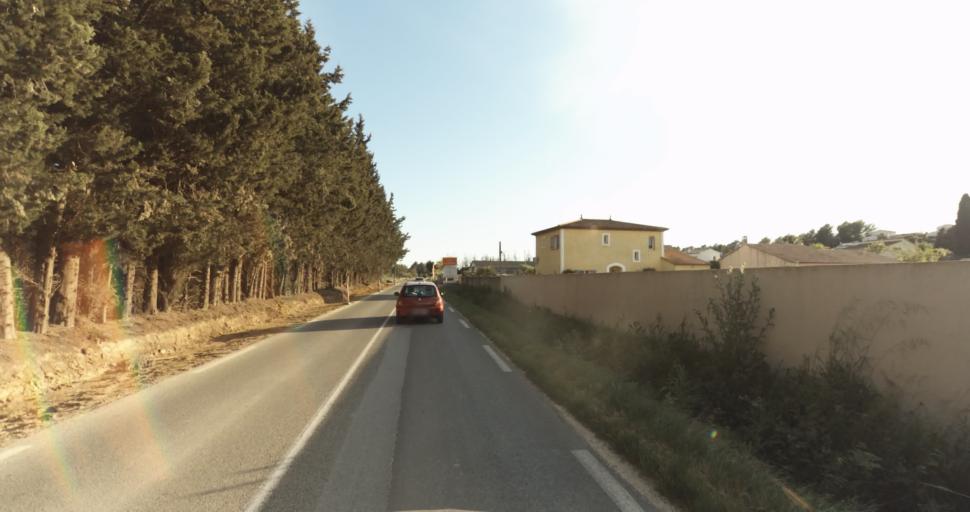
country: FR
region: Provence-Alpes-Cote d'Azur
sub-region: Departement du Var
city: La Crau
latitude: 43.1611
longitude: 6.0990
